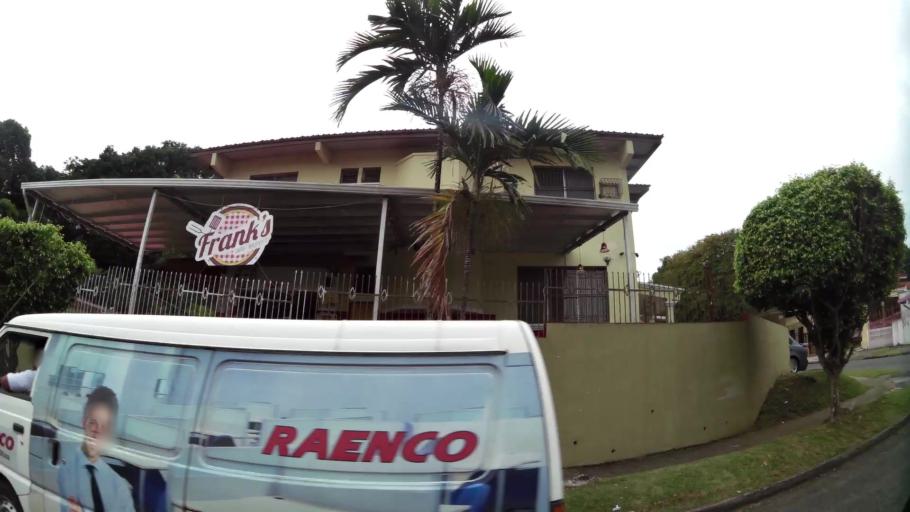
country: PA
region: Panama
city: Panama
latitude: 9.0172
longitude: -79.5236
